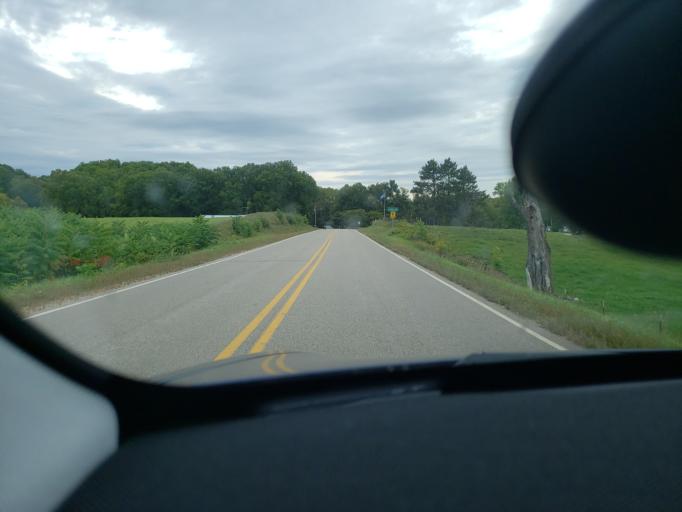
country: US
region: Wisconsin
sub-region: Waupaca County
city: Marion
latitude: 44.7174
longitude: -88.8827
